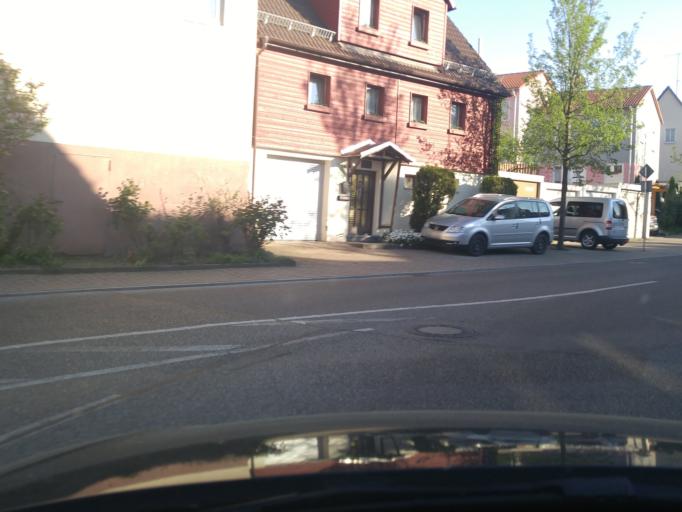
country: DE
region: Baden-Wuerttemberg
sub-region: Regierungsbezirk Stuttgart
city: Cleebronn
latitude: 49.0441
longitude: 9.0371
